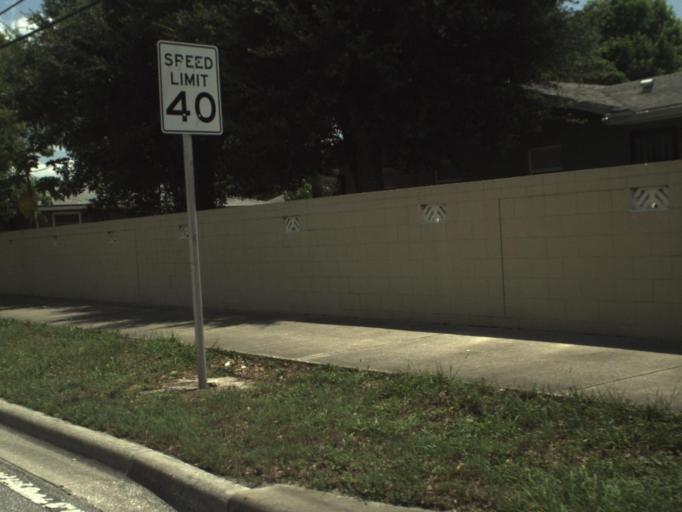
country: US
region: Florida
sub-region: Orange County
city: Conway
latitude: 28.5325
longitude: -81.3311
